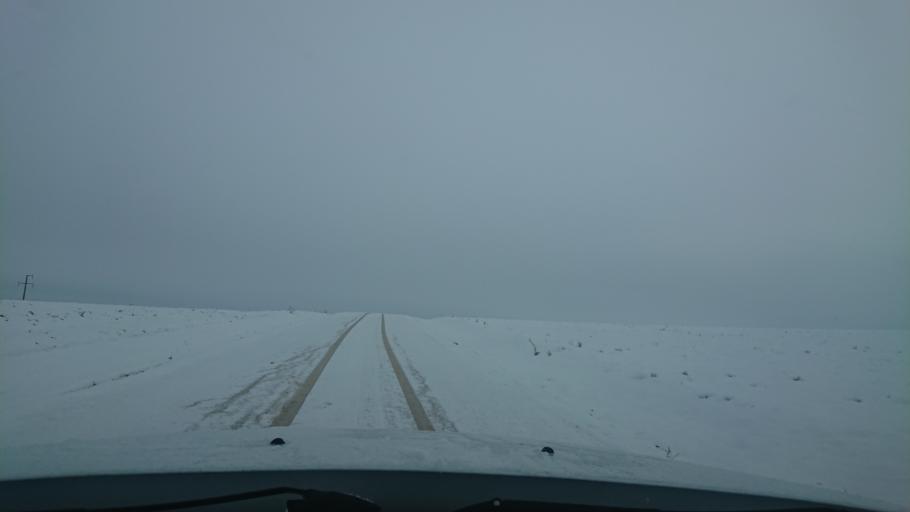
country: TR
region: Aksaray
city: Agacoren
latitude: 38.7393
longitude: 33.8705
